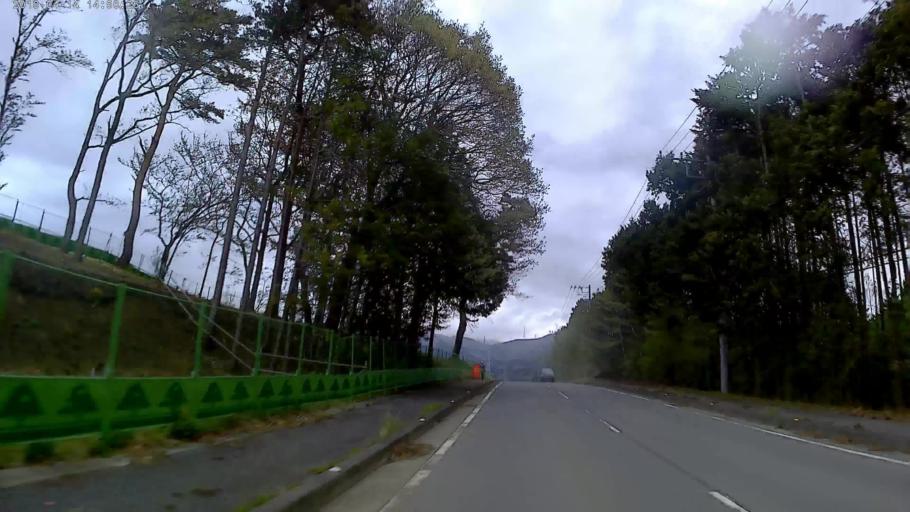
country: JP
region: Shizuoka
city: Gotemba
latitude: 35.3656
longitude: 138.9665
